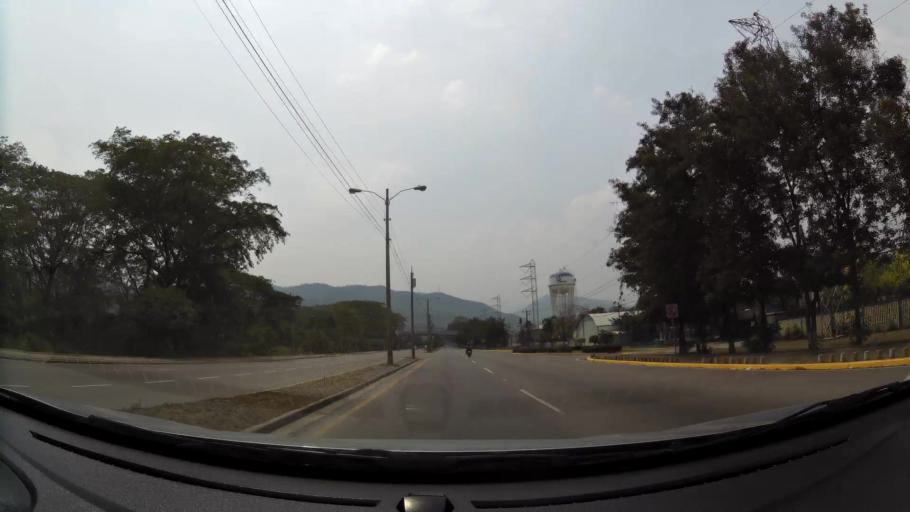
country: HN
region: Cortes
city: Nuevo Chamelecon
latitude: 15.4055
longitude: -88.0067
